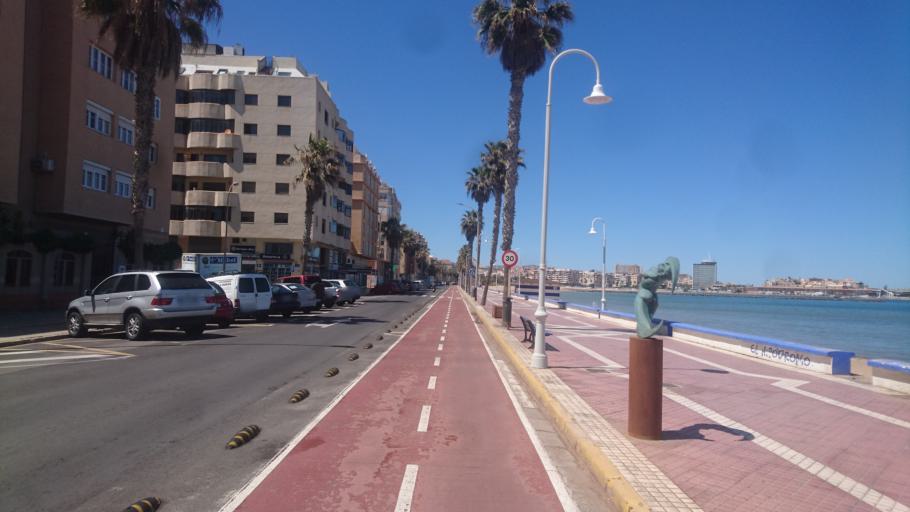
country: ES
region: Melilla
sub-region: Melilla
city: Melilla
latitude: 35.2788
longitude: -2.9360
